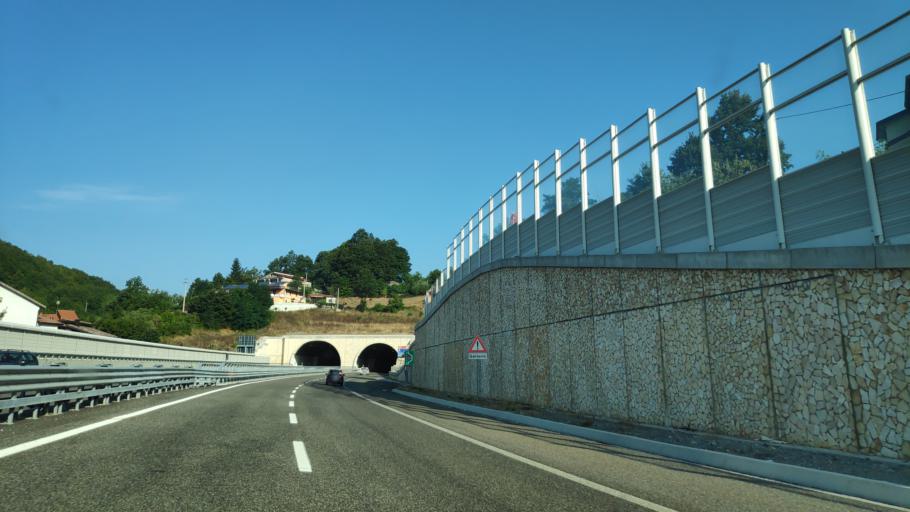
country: IT
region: Basilicate
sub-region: Provincia di Potenza
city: Lauria
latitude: 40.0206
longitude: 15.8819
